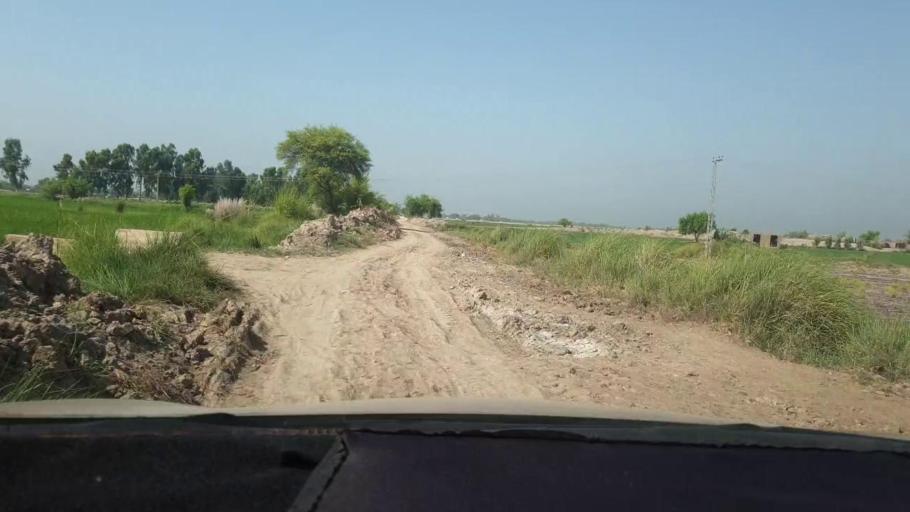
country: PK
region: Sindh
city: Miro Khan
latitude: 27.7158
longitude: 68.1070
